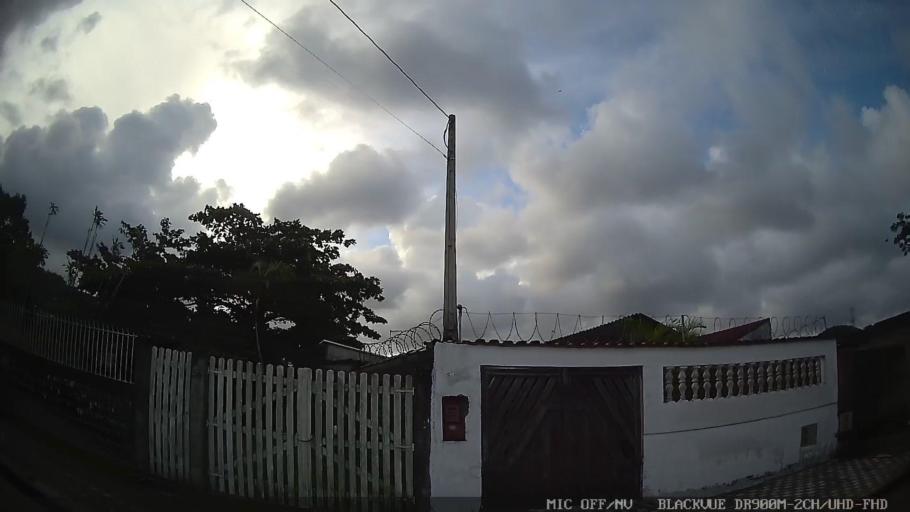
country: BR
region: Sao Paulo
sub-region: Mongagua
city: Mongagua
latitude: -24.1198
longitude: -46.6763
